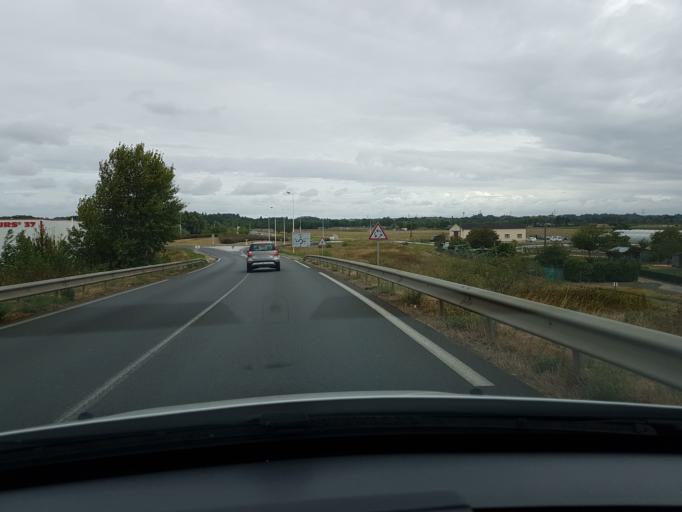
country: FR
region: Centre
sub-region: Departement d'Indre-et-Loire
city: La Ville-aux-Dames
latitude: 47.3918
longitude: 0.7882
